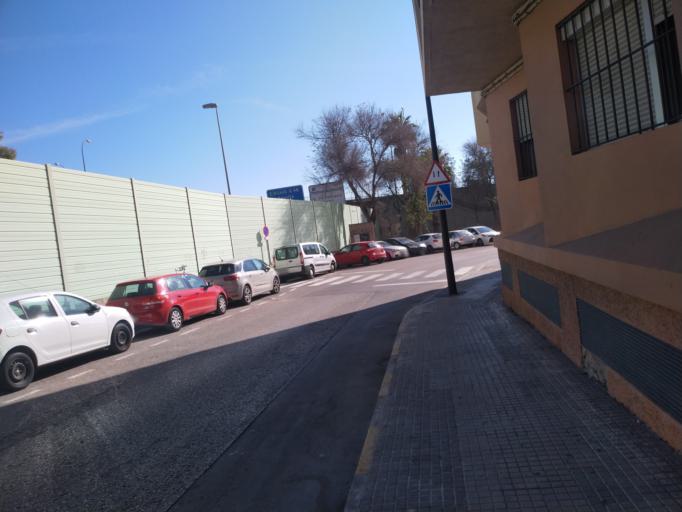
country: ES
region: Andalusia
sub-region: Provincia de Cadiz
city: San Fernando
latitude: 36.4723
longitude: -6.1899
